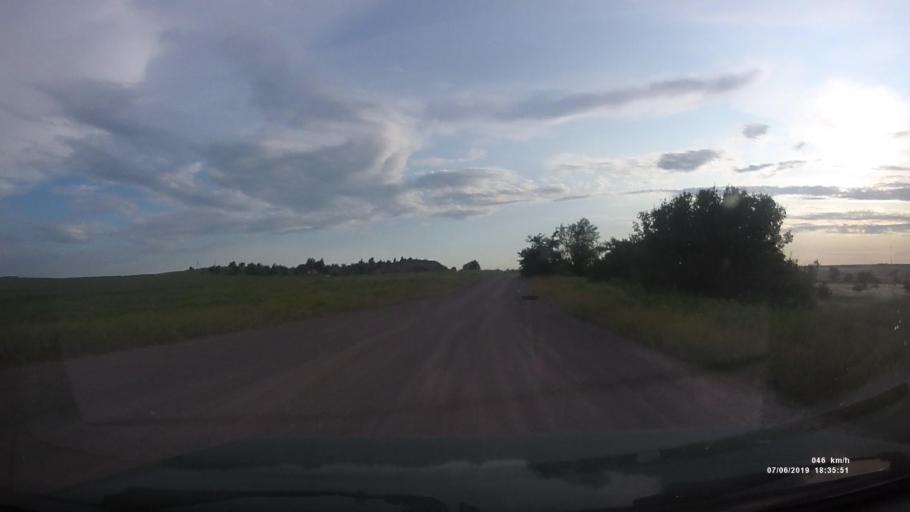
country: RU
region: Rostov
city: Staraya Stanitsa
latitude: 48.2539
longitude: 40.3553
